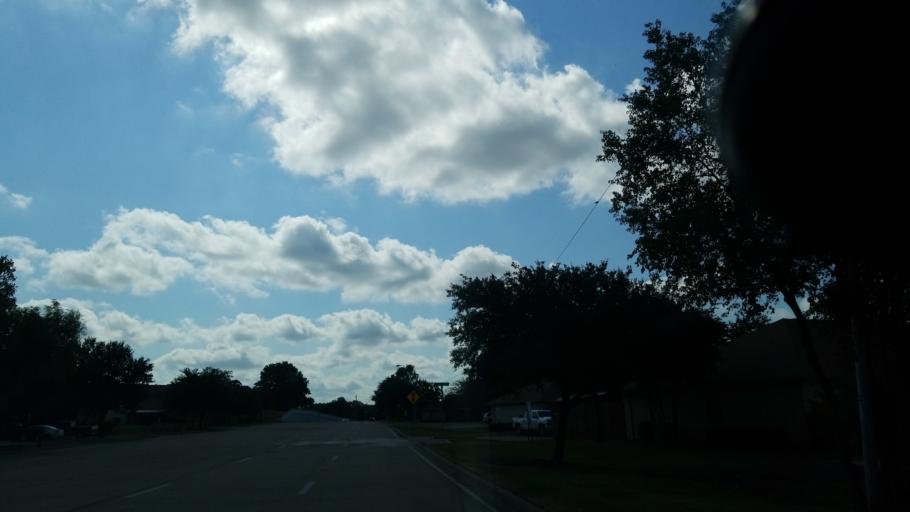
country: US
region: Texas
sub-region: Dallas County
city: Grand Prairie
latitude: 32.6963
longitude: -96.9885
